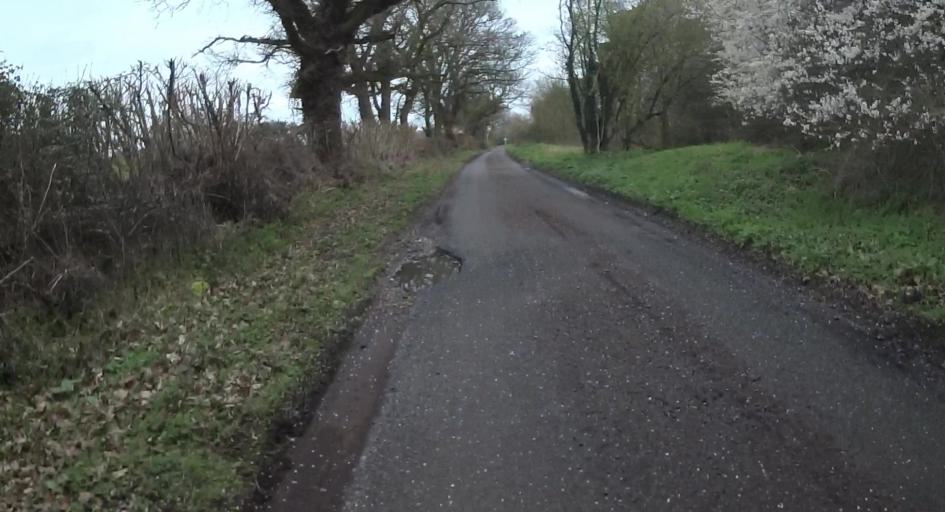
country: GB
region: England
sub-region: Hampshire
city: Overton
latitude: 51.2623
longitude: -1.2430
